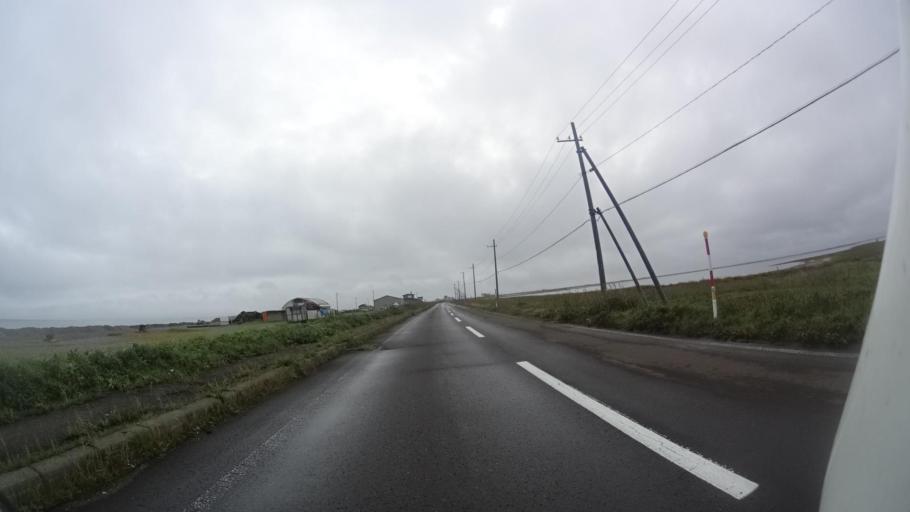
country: JP
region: Hokkaido
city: Shibetsu
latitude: 43.5970
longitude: 145.3217
